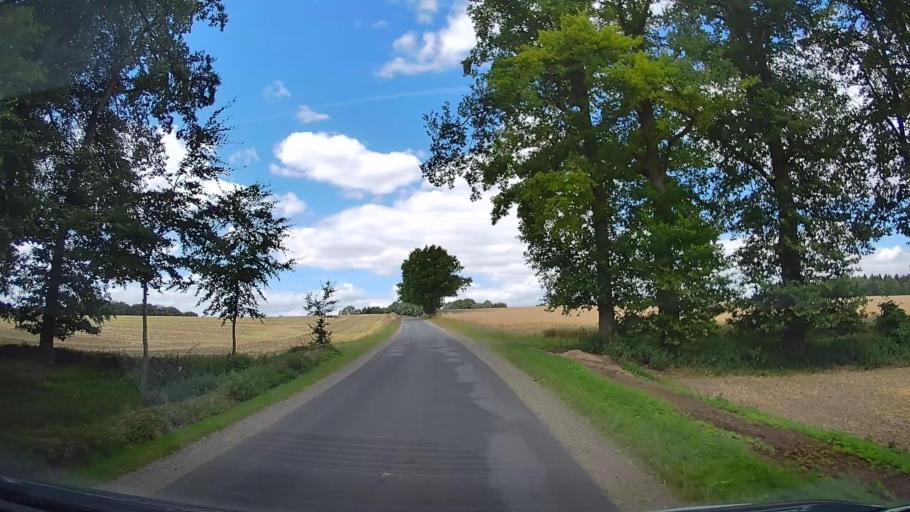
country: DE
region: Lower Saxony
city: Belm
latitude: 52.3821
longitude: 8.1395
